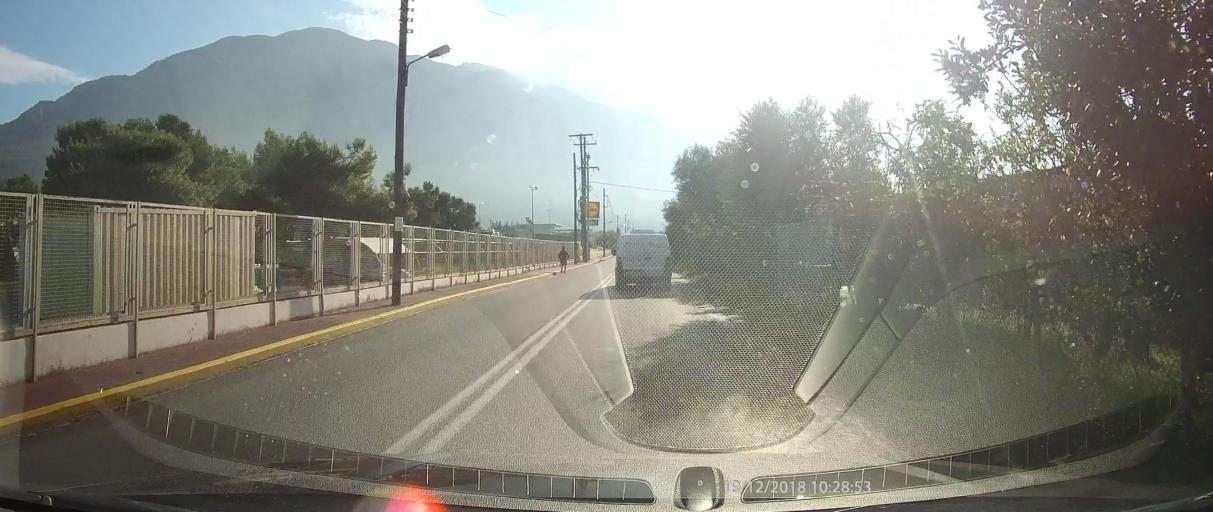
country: GR
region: Peloponnese
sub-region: Nomos Messinias
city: Paralia Vergas
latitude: 37.0260
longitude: 22.1437
